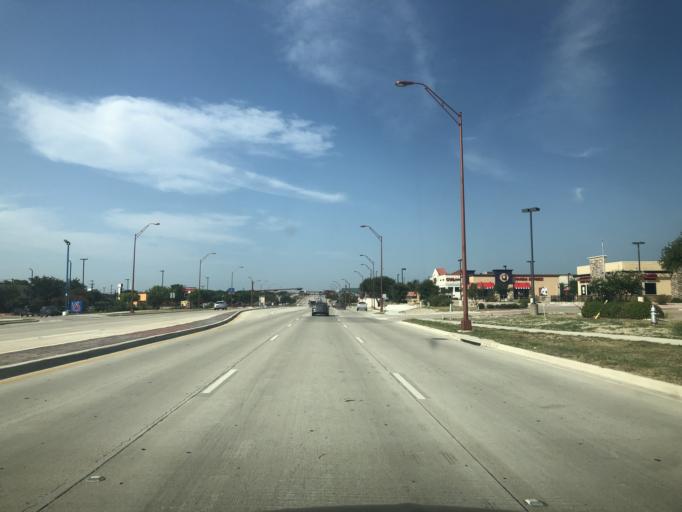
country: US
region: Texas
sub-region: Tarrant County
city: Benbrook
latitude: 32.6809
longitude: -97.4626
